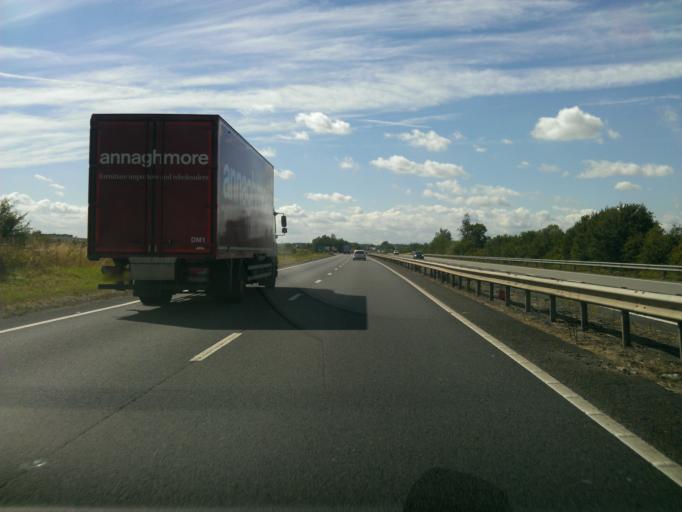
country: GB
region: England
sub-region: Bedford
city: Pertenhall
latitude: 52.3632
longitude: -0.4249
